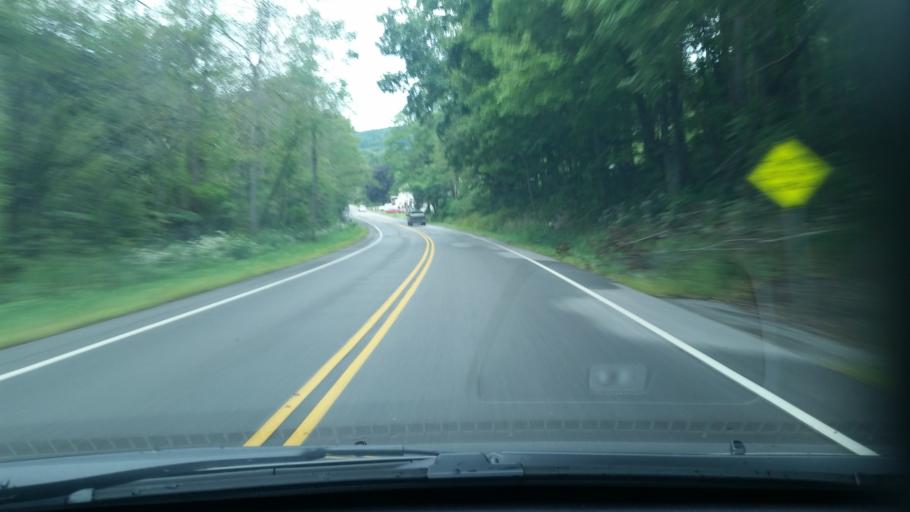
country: US
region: Pennsylvania
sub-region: Clearfield County
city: Shiloh
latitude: 41.0776
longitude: -78.3312
